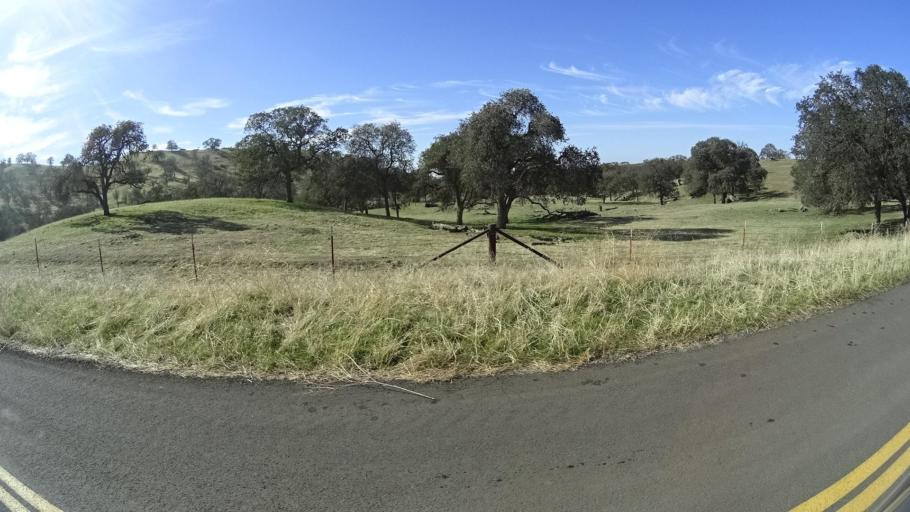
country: US
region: California
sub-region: Tulare County
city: Richgrove
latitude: 35.6734
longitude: -118.8525
